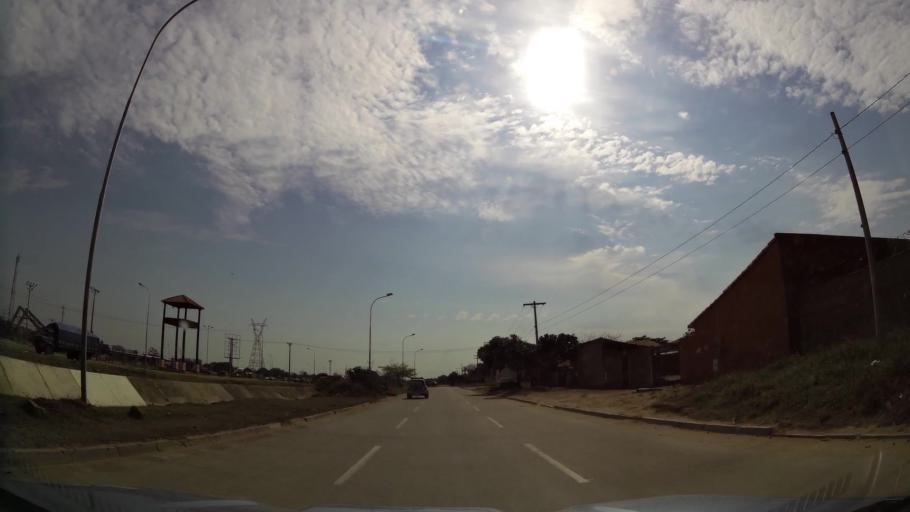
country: BO
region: Santa Cruz
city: Santa Cruz de la Sierra
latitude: -17.7293
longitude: -63.1360
